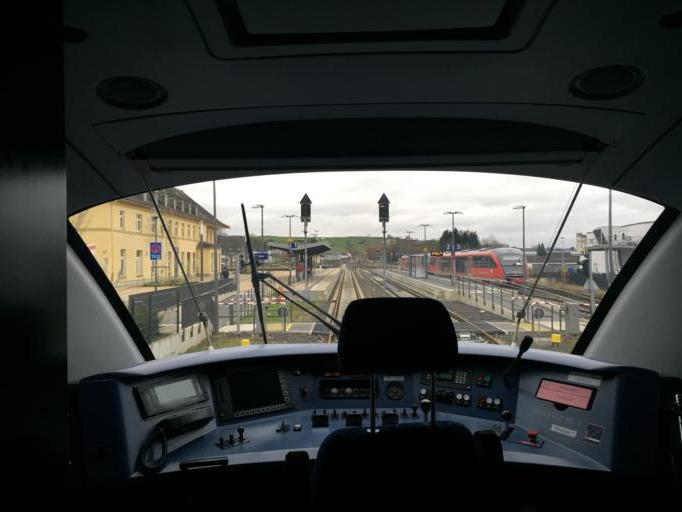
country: DE
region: Hesse
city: Frankenberg
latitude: 51.0550
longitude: 8.7898
